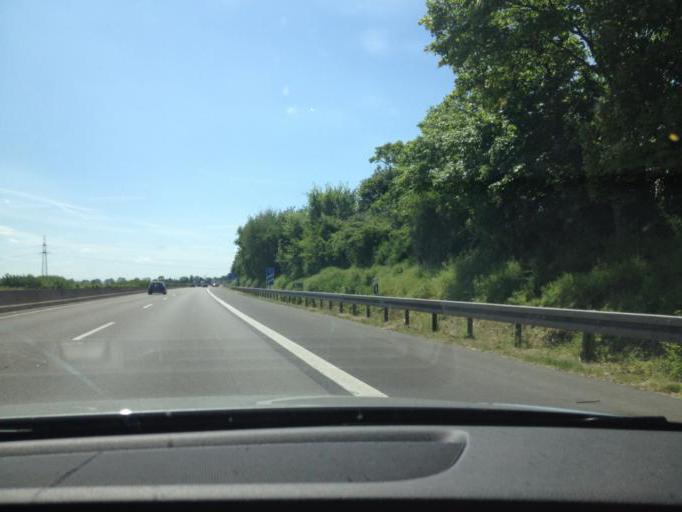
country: DE
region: North Rhine-Westphalia
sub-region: Regierungsbezirk Koln
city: Weilerswist
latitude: 50.7552
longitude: 6.8143
